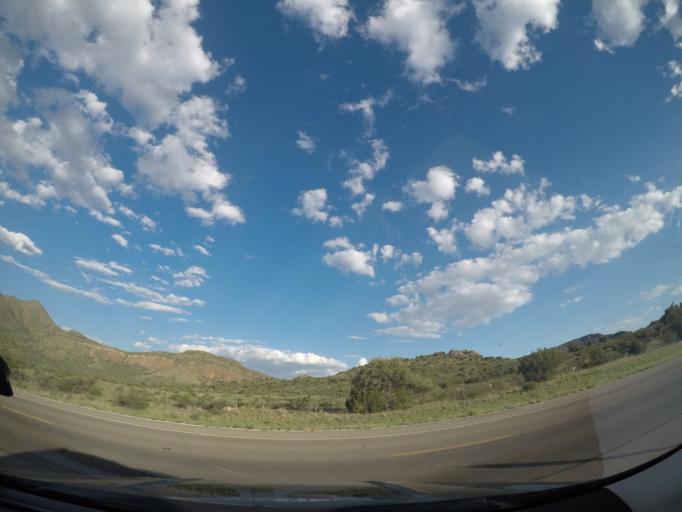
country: US
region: Texas
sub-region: Brewster County
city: Alpine
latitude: 30.3223
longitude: -103.7434
